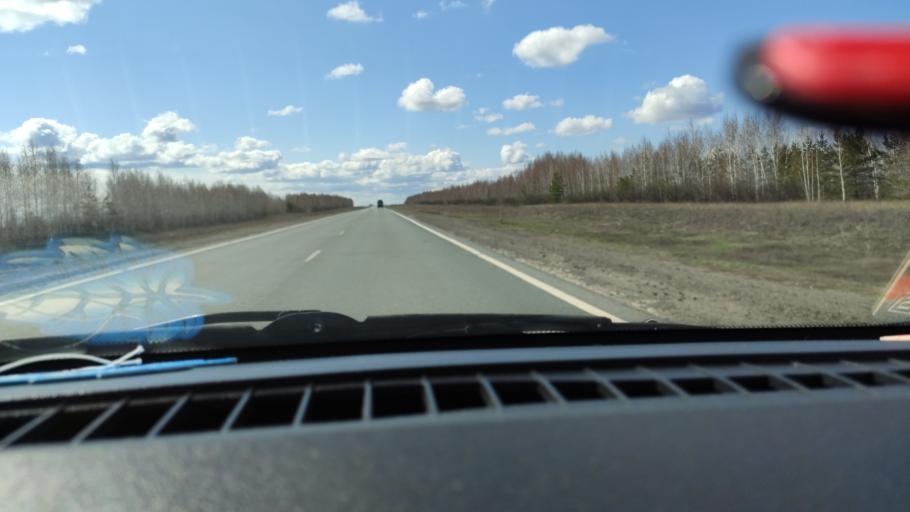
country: RU
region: Saratov
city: Dukhovnitskoye
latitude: 52.8152
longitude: 48.2314
